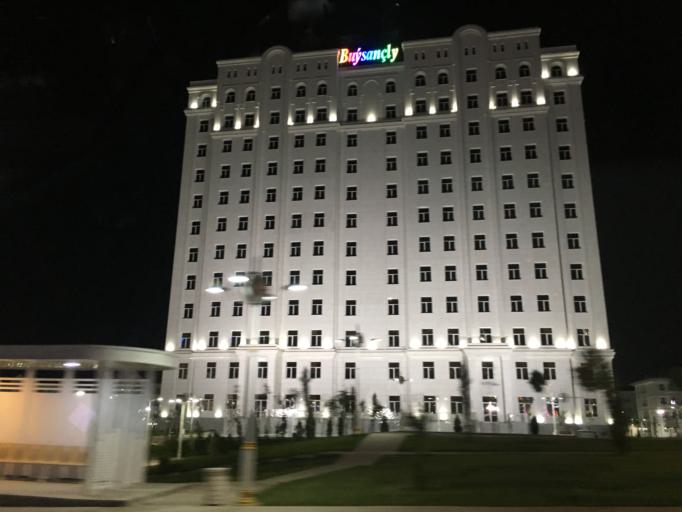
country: TM
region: Ahal
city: Ashgabat
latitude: 37.9403
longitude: 58.3531
